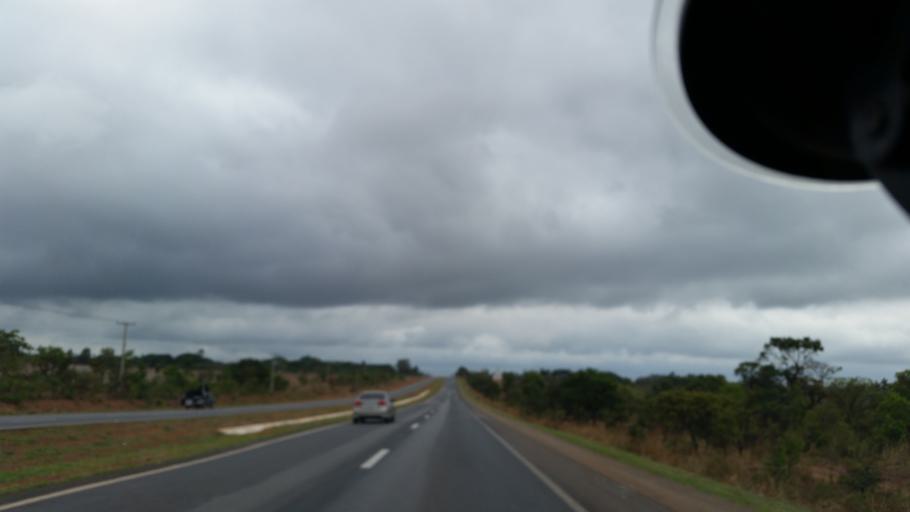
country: BR
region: Goias
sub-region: Luziania
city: Luziania
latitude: -16.3088
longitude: -47.8430
